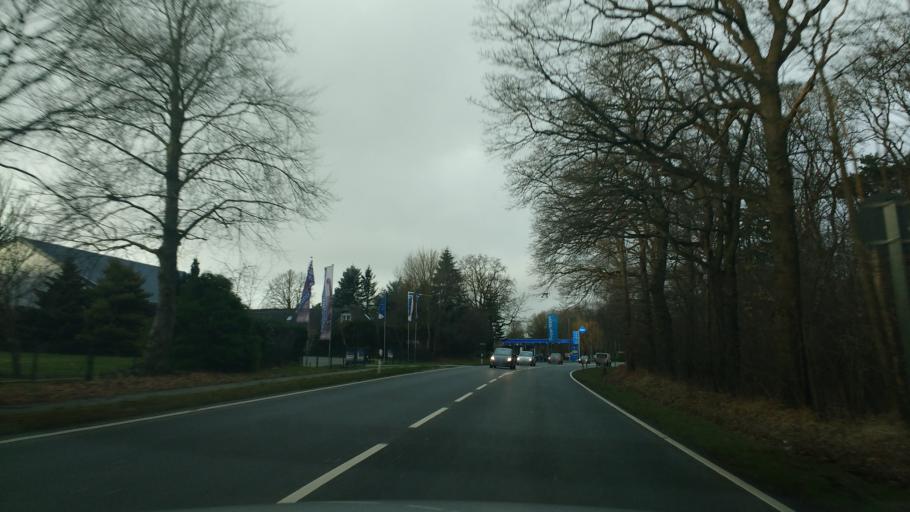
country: DE
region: Schleswig-Holstein
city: Itzehoe
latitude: 53.9042
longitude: 9.5089
